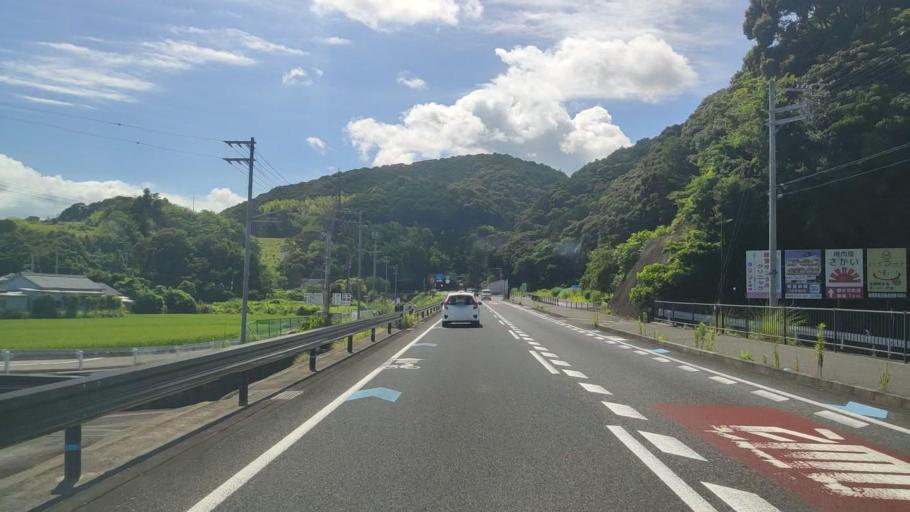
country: JP
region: Wakayama
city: Shingu
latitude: 33.7405
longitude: 135.9977
